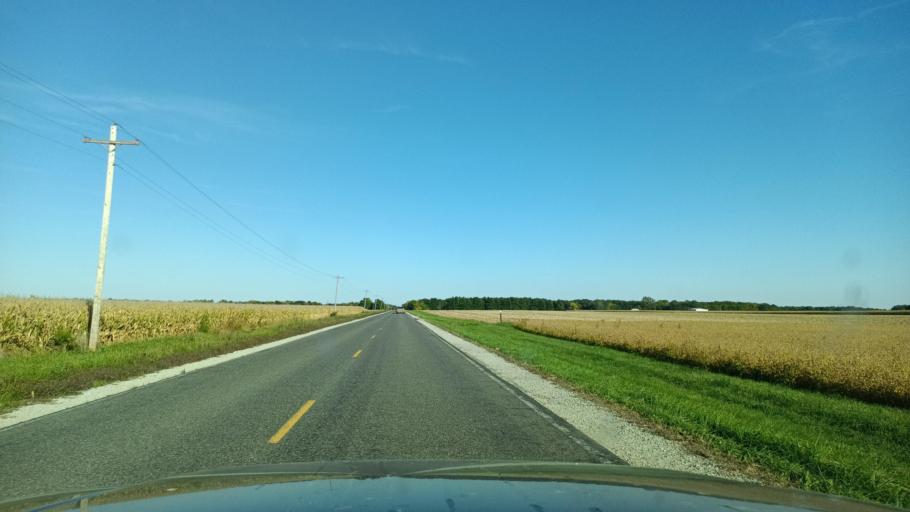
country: US
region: Illinois
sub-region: De Witt County
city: Clinton
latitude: 40.2245
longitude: -88.8455
